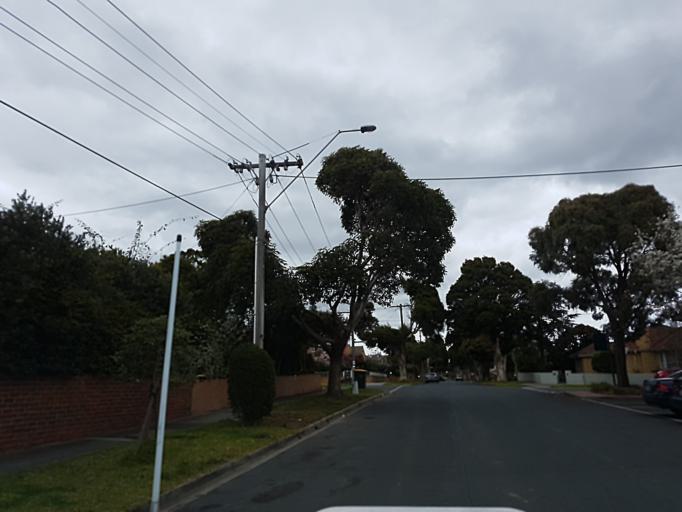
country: AU
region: Victoria
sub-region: Whitehorse
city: Box Hill North
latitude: -37.8009
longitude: 145.1395
